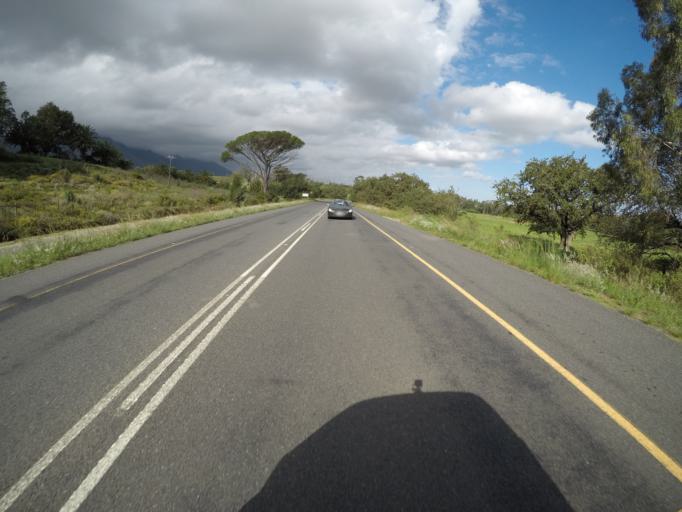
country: ZA
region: Western Cape
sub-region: Overberg District Municipality
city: Swellendam
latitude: -34.0110
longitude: 20.3885
